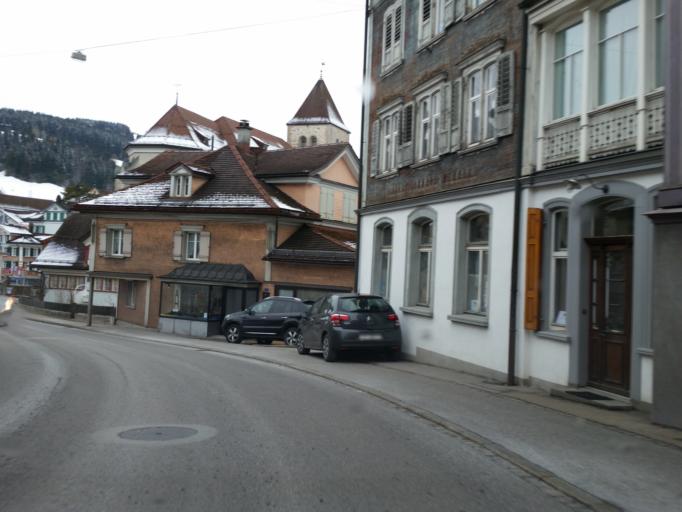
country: CH
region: Appenzell Innerrhoden
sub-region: Appenzell Inner Rhodes
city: Appenzell
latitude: 47.3317
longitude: 9.4117
